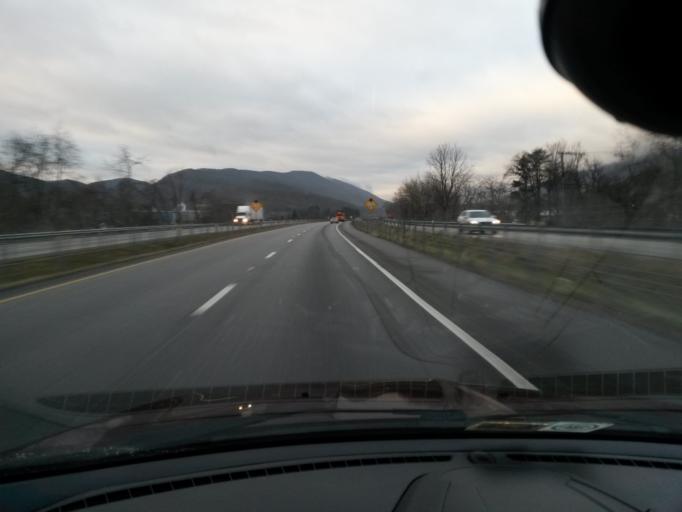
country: US
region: Virginia
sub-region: Alleghany County
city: Clifton Forge
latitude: 37.7974
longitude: -79.8743
